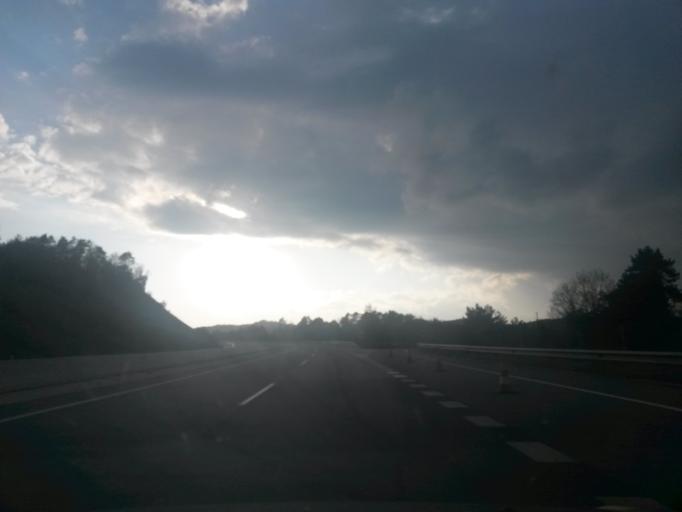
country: ES
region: Catalonia
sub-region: Provincia de Girona
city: Viladrau
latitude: 41.8954
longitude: 2.3718
